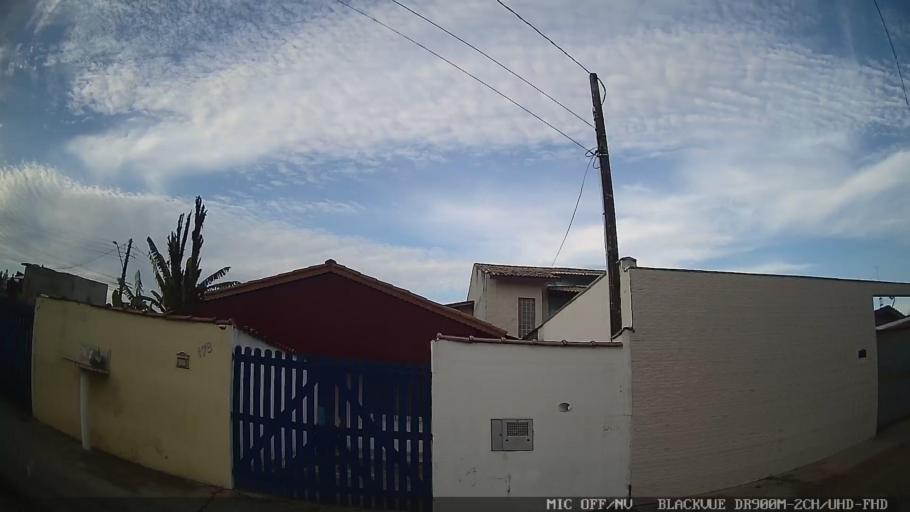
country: BR
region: Sao Paulo
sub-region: Itanhaem
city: Itanhaem
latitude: -24.1698
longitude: -46.7741
